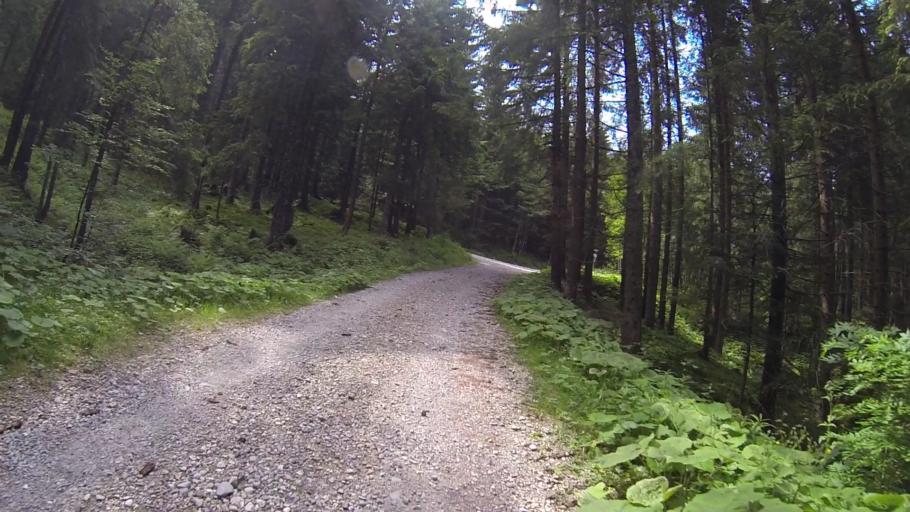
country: AT
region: Tyrol
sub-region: Politischer Bezirk Reutte
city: Jungholz
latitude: 47.5922
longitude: 10.4720
